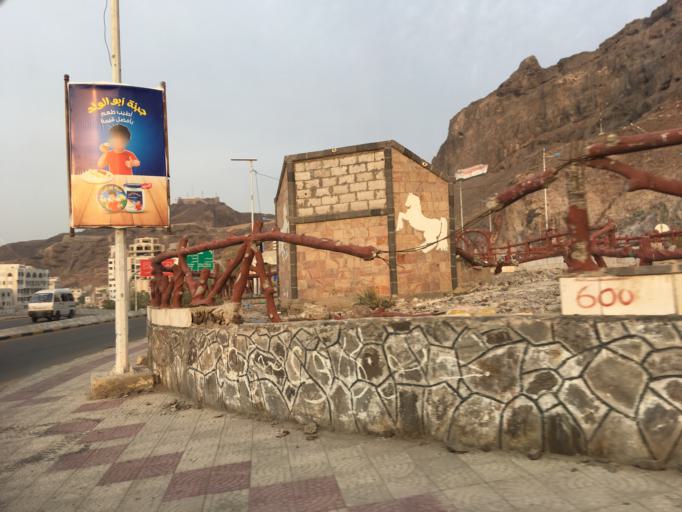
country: YE
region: Aden
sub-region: Craiter
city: Crater
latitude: 12.7890
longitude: 45.0208
